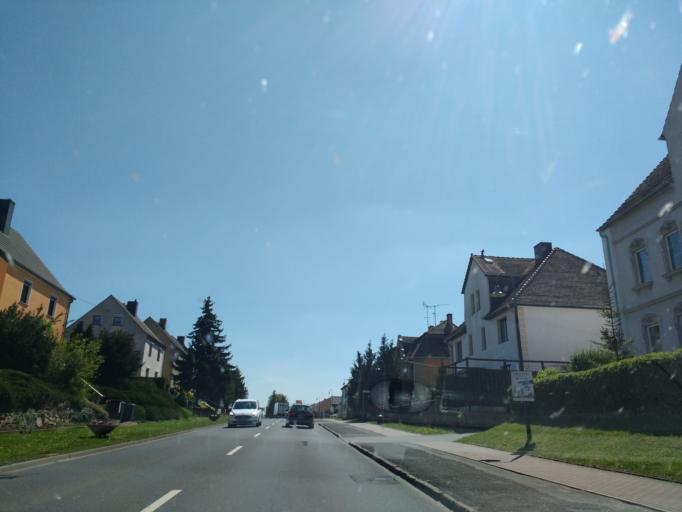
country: DE
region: Saxony-Anhalt
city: Theissen
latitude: 51.0854
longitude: 12.1090
